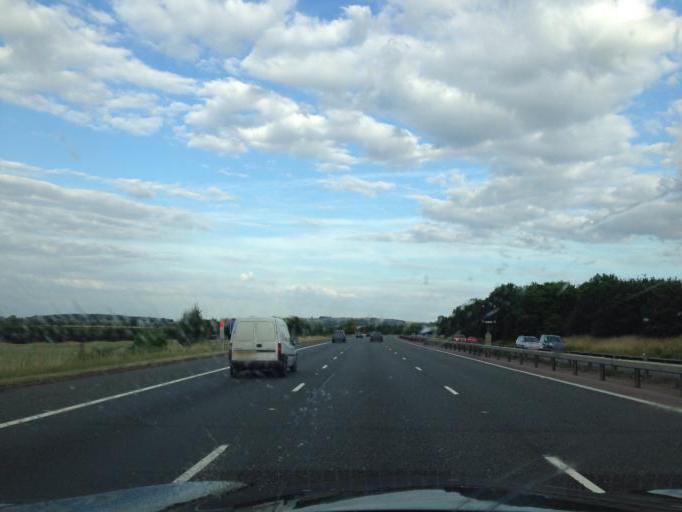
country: GB
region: England
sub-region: Oxfordshire
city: Bicester
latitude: 51.8443
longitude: -1.1537
